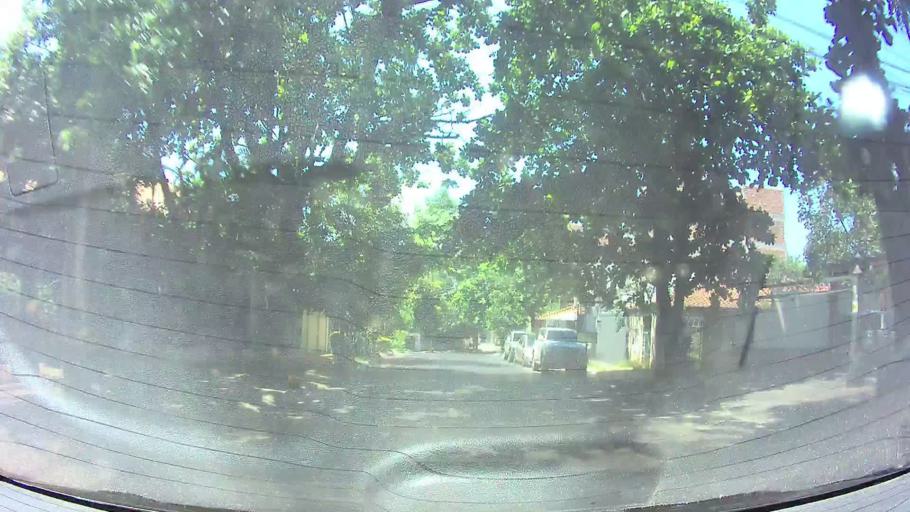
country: PY
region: Asuncion
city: Asuncion
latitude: -25.2990
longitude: -57.5885
